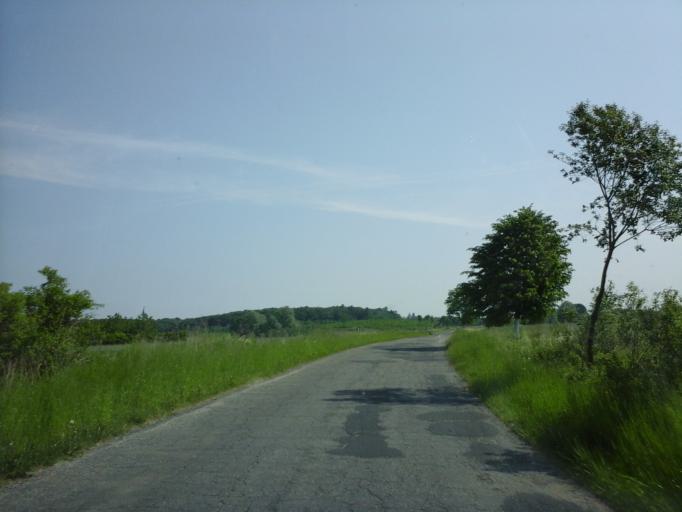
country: PL
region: West Pomeranian Voivodeship
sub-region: Powiat stargardzki
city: Dobrzany
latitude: 53.3643
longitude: 15.4442
